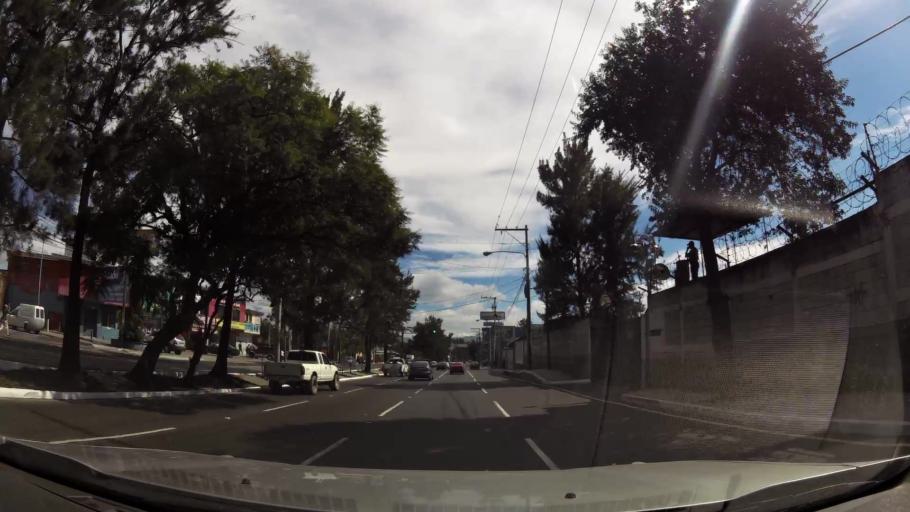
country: GT
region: Guatemala
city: Guatemala City
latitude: 14.6335
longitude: -90.5595
